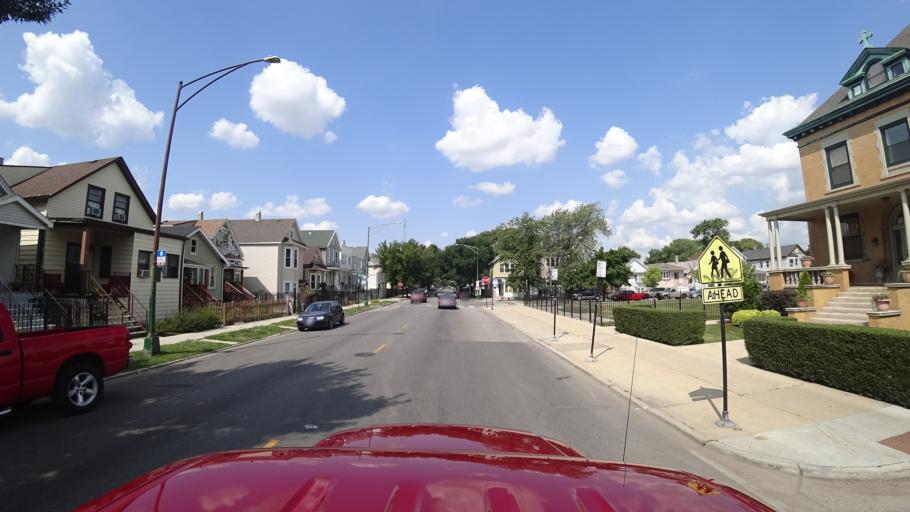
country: US
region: Illinois
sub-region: Cook County
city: Chicago
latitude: 41.8229
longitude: -87.6916
